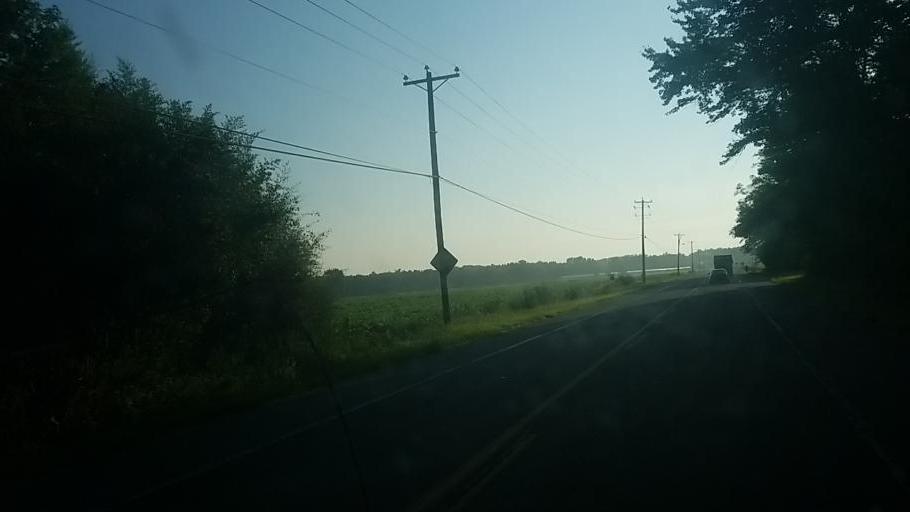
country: US
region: Delaware
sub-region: Sussex County
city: Selbyville
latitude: 38.4598
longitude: -75.1968
